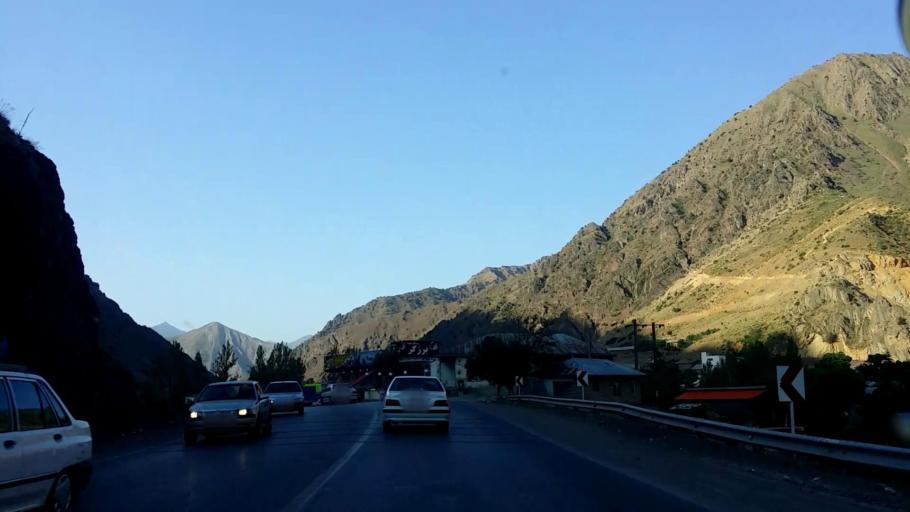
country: IR
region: Tehran
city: Tajrish
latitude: 36.0711
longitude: 51.3094
